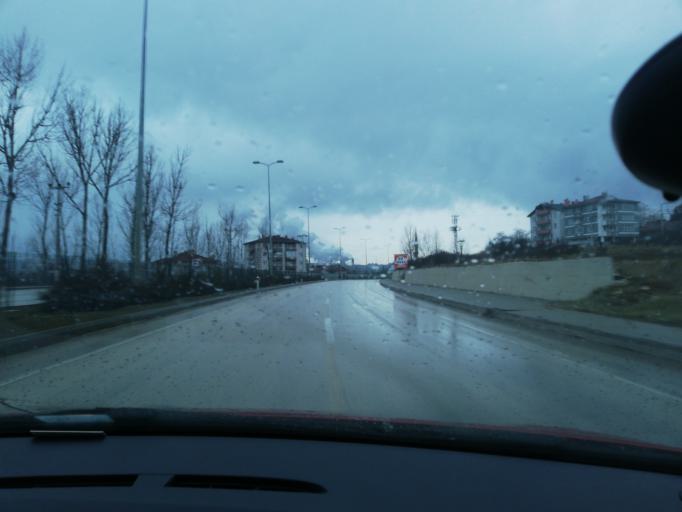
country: TR
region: Kastamonu
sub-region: Cide
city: Kastamonu
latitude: 41.4209
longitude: 33.8020
